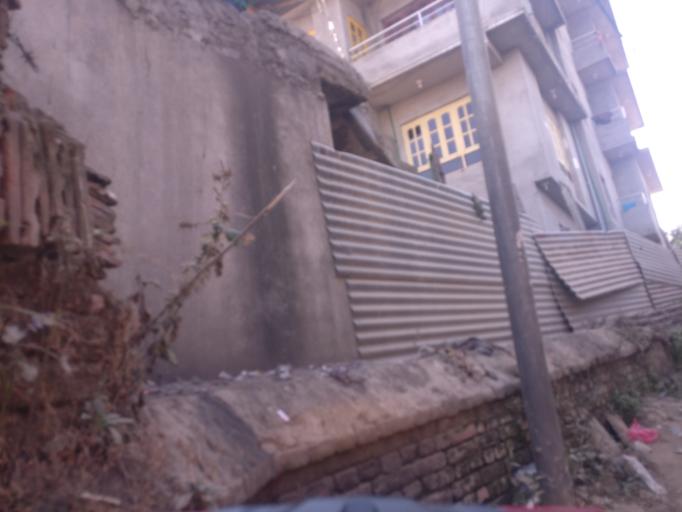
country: NP
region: Central Region
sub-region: Bagmati Zone
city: Patan
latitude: 27.6785
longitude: 85.3311
